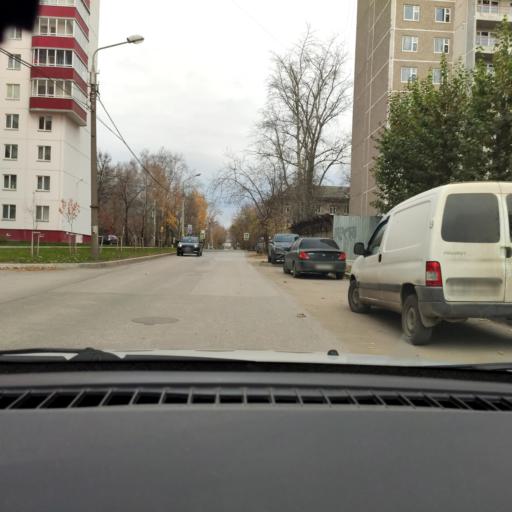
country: RU
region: Perm
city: Kondratovo
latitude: 58.0337
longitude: 56.0285
